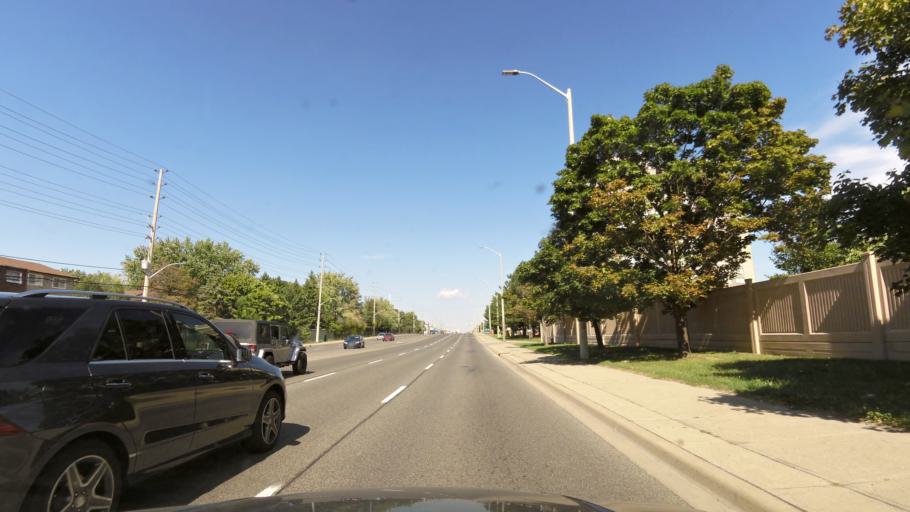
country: CA
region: Ontario
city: Mississauga
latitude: 43.5608
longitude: -79.6386
